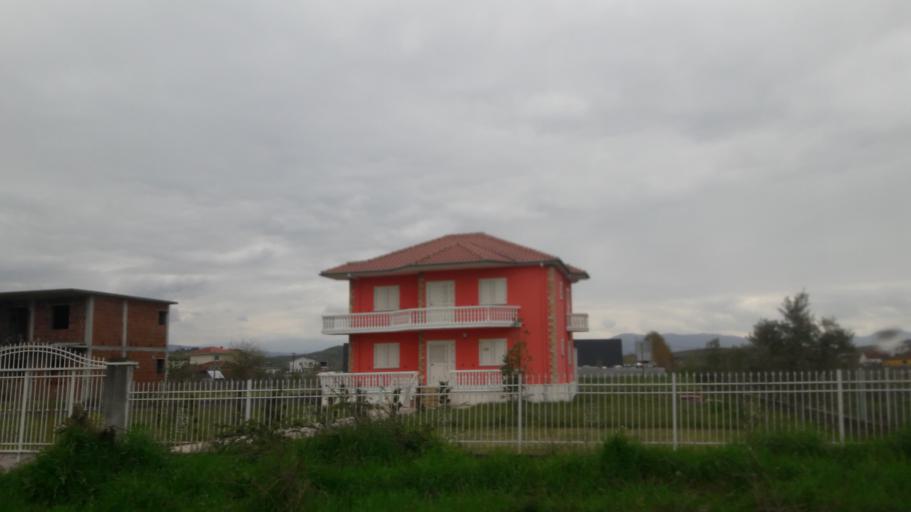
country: AL
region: Shkoder
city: Vukatane
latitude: 41.9707
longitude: 19.5398
